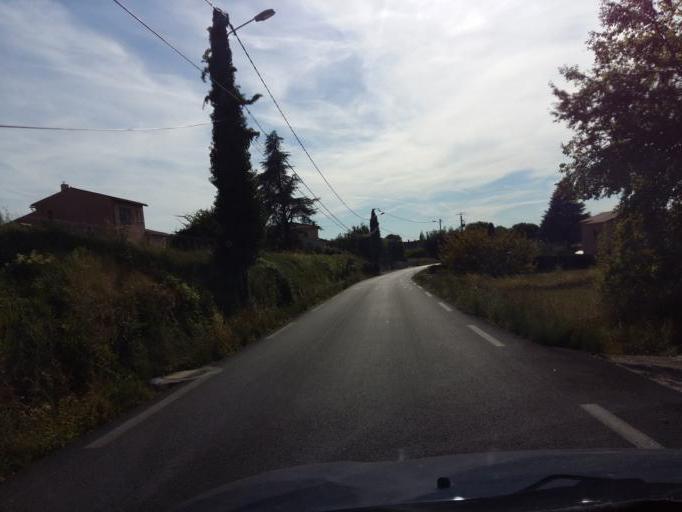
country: FR
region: Provence-Alpes-Cote d'Azur
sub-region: Departement du Vaucluse
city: Saint-Didier
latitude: 44.0066
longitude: 5.1190
